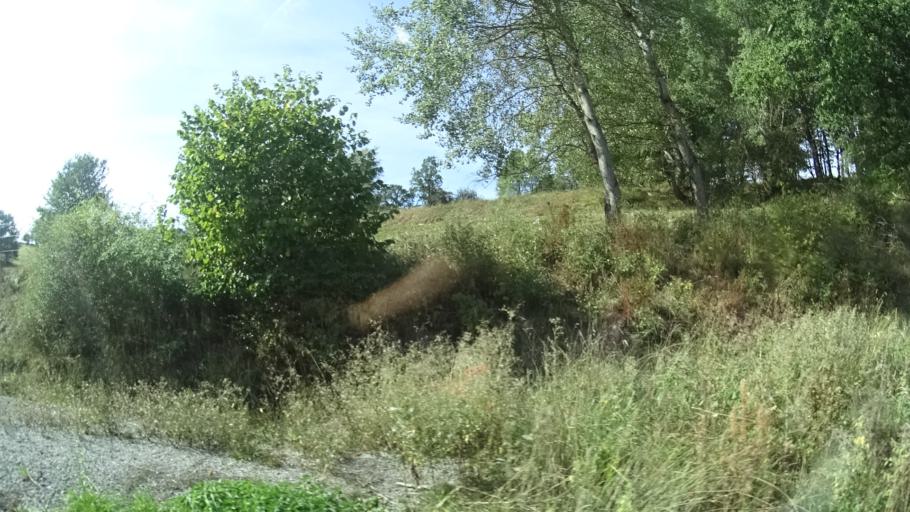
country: DE
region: Thuringia
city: Metzels
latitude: 50.6546
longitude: 10.4392
